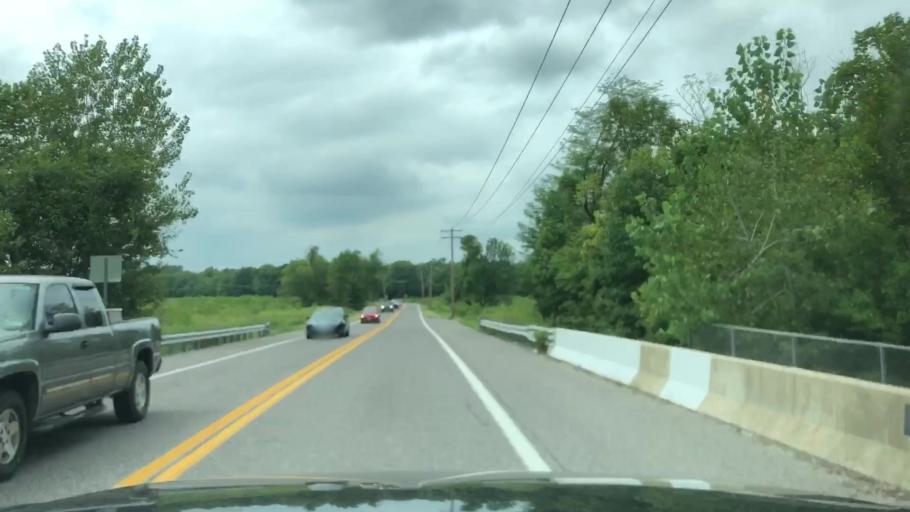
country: US
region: Missouri
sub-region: Saint Louis County
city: Hazelwood
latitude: 38.8111
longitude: -90.3913
